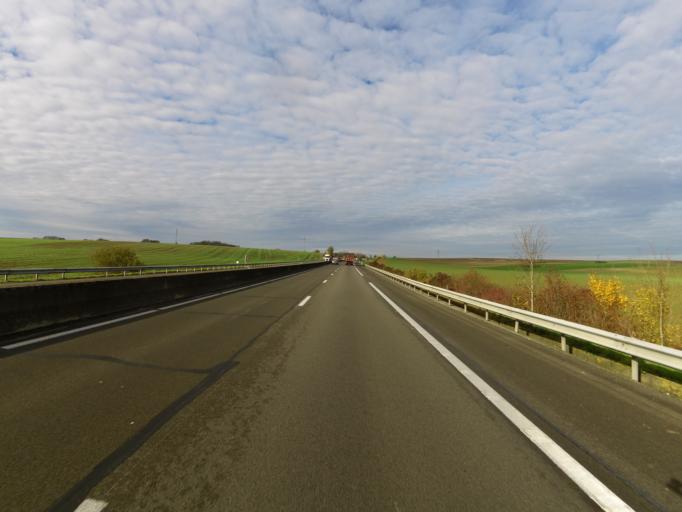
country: FR
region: Picardie
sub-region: Departement de l'Aisne
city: Itancourt
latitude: 49.7594
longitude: 3.3675
